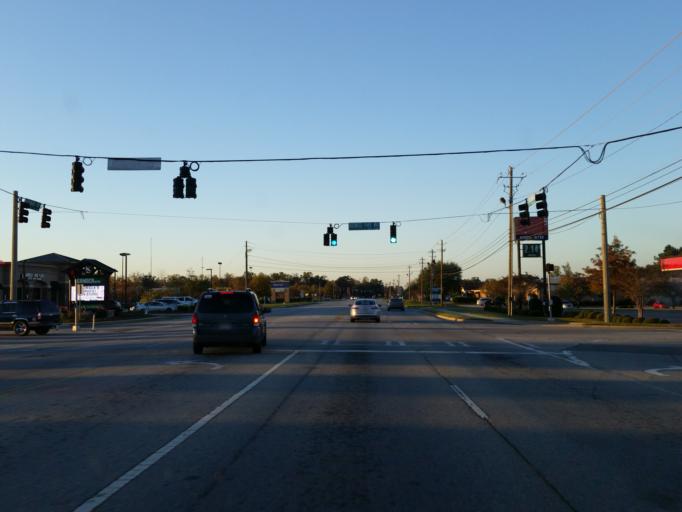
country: US
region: Georgia
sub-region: Lowndes County
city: Remerton
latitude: 30.8250
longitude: -83.3164
